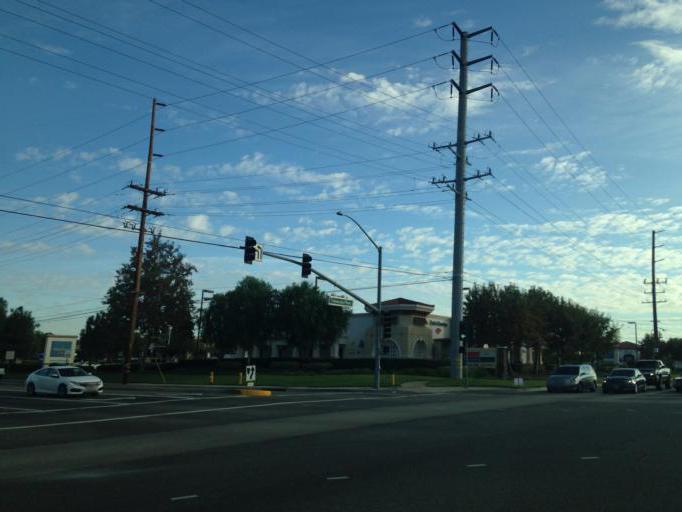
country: US
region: California
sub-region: Riverside County
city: Temecula
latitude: 33.4803
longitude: -117.1017
